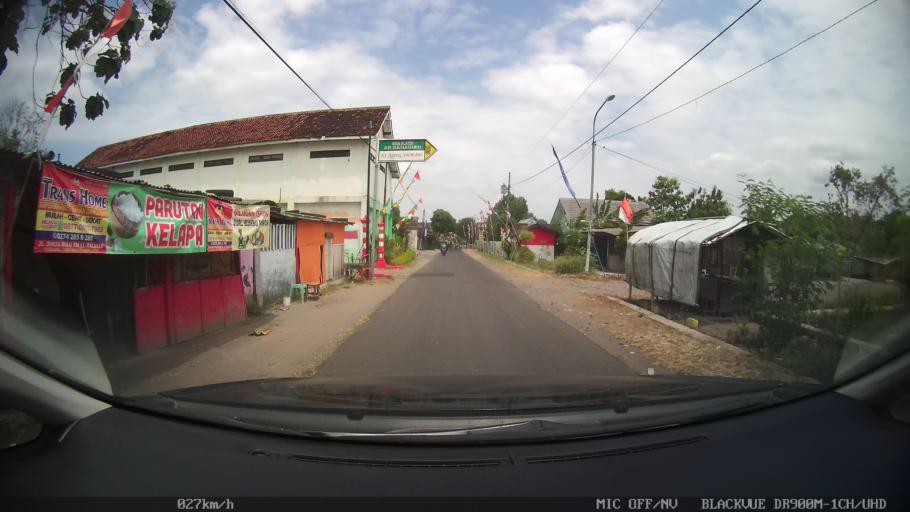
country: ID
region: Central Java
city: Candi Prambanan
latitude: -7.7740
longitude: 110.4786
